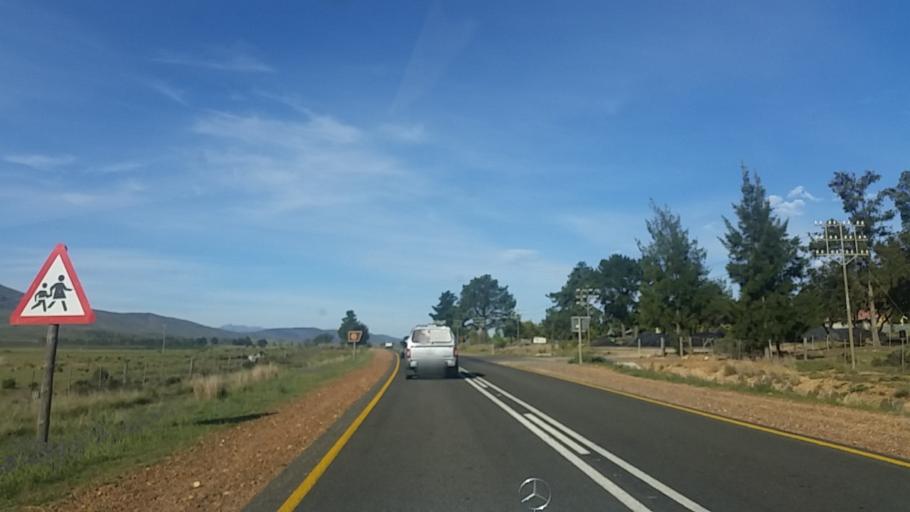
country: ZA
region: Western Cape
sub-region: Eden District Municipality
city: George
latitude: -33.8337
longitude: 22.4510
